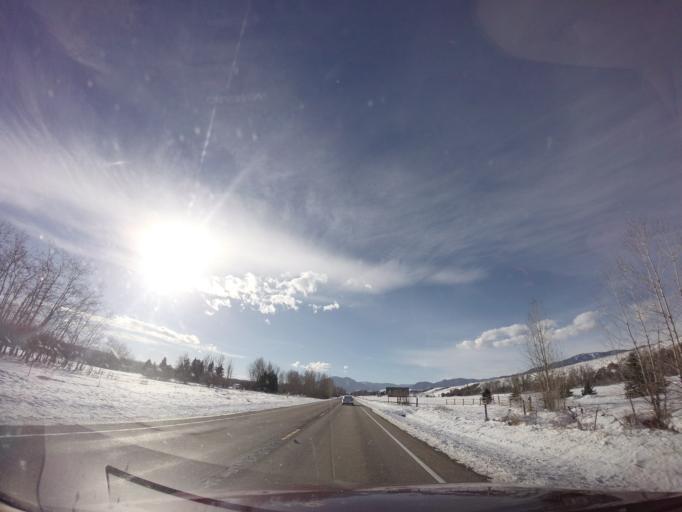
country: US
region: Montana
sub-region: Carbon County
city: Red Lodge
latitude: 45.2464
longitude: -109.2347
